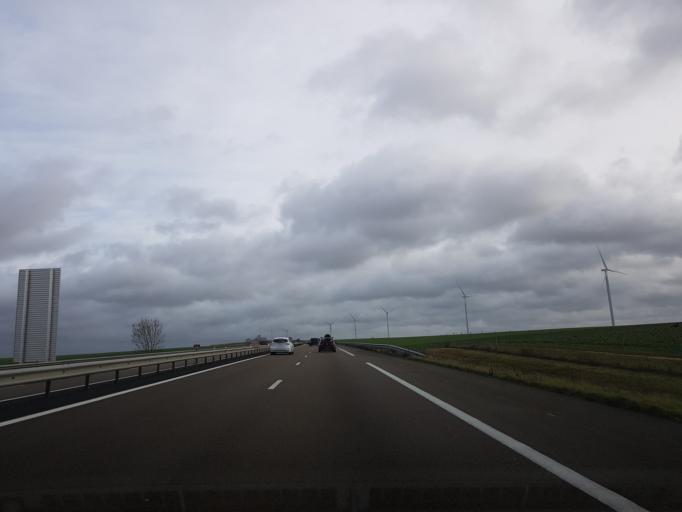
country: FR
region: Champagne-Ardenne
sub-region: Departement de l'Aube
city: Vendeuvre-sur-Barse
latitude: 48.1664
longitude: 4.4941
